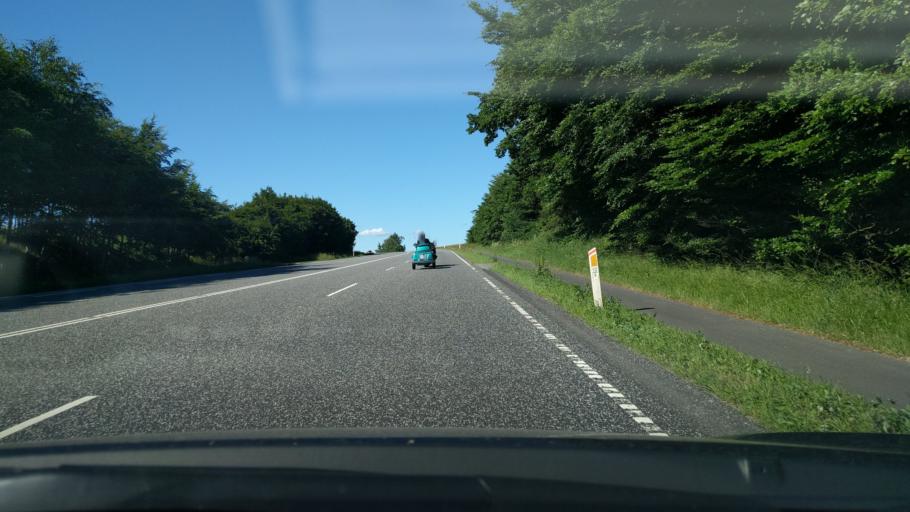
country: DK
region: Central Jutland
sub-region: Viborg Kommune
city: Viborg
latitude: 56.5534
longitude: 9.4820
